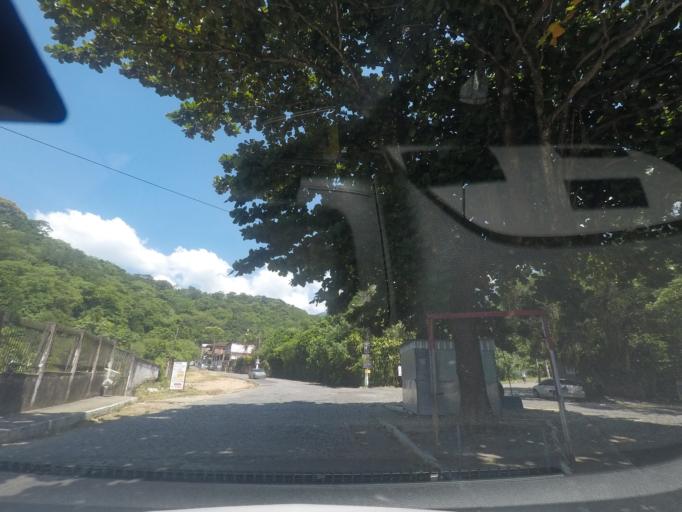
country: BR
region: Rio de Janeiro
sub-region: Petropolis
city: Petropolis
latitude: -22.5701
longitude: -43.1846
